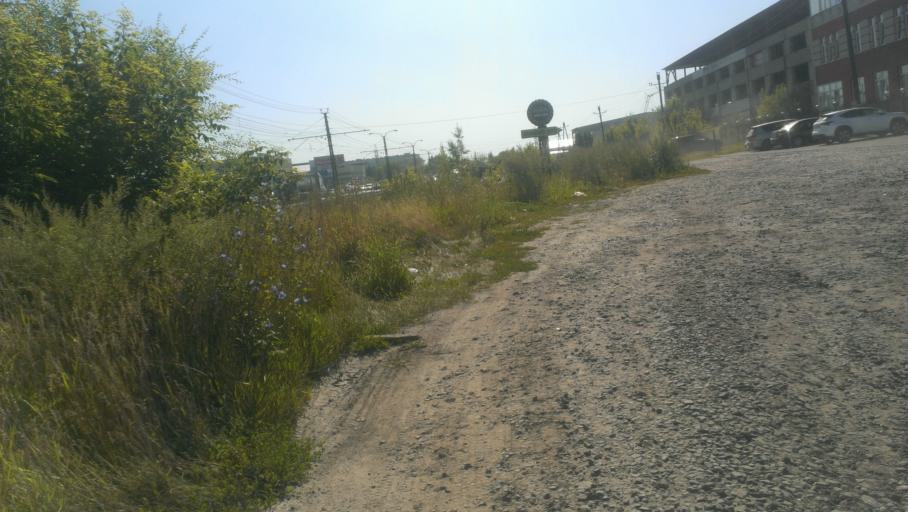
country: RU
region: Altai Krai
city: Novosilikatnyy
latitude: 53.3281
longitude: 83.6576
